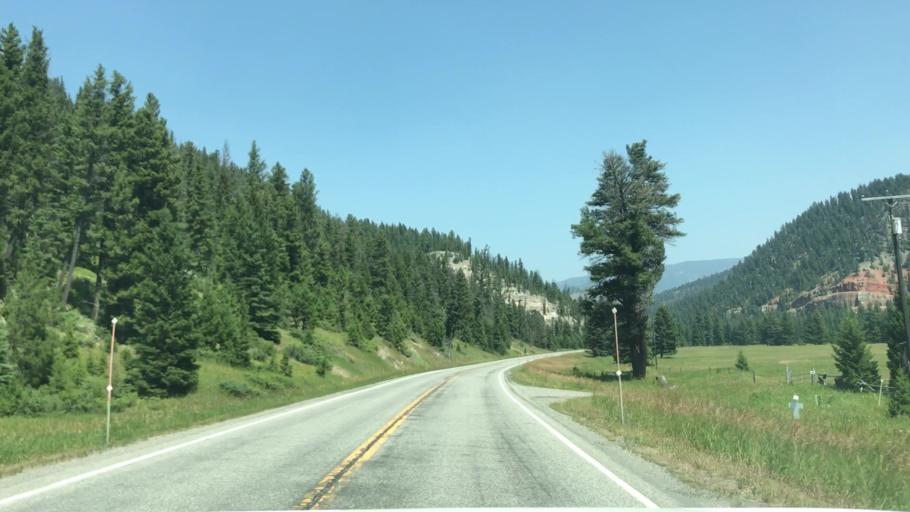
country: US
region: Montana
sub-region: Gallatin County
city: Big Sky
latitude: 45.1630
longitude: -111.2486
